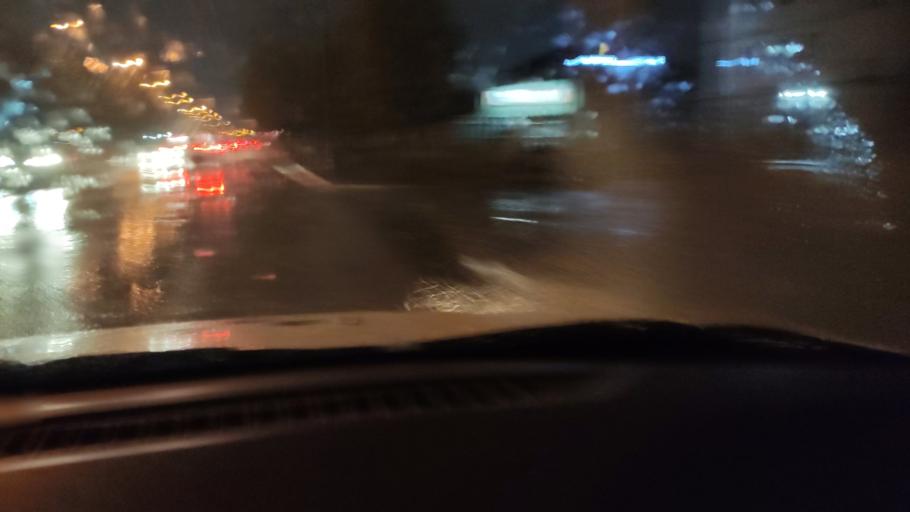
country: RU
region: Perm
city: Perm
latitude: 57.9772
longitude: 56.2464
